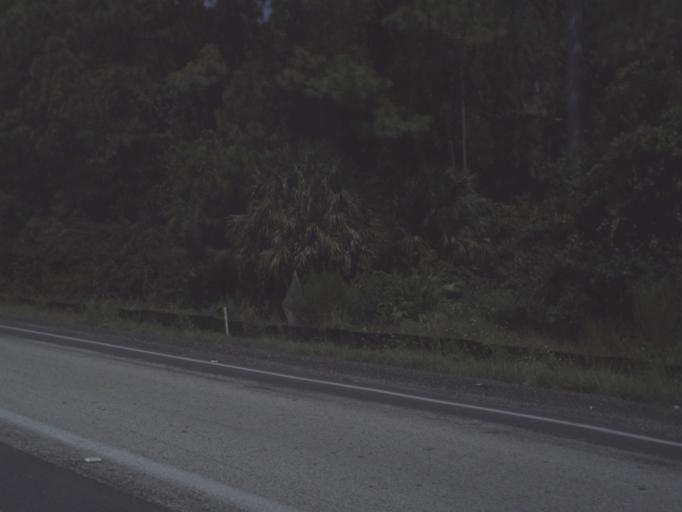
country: US
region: Florida
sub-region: Sarasota County
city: North Port
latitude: 27.0991
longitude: -82.1603
